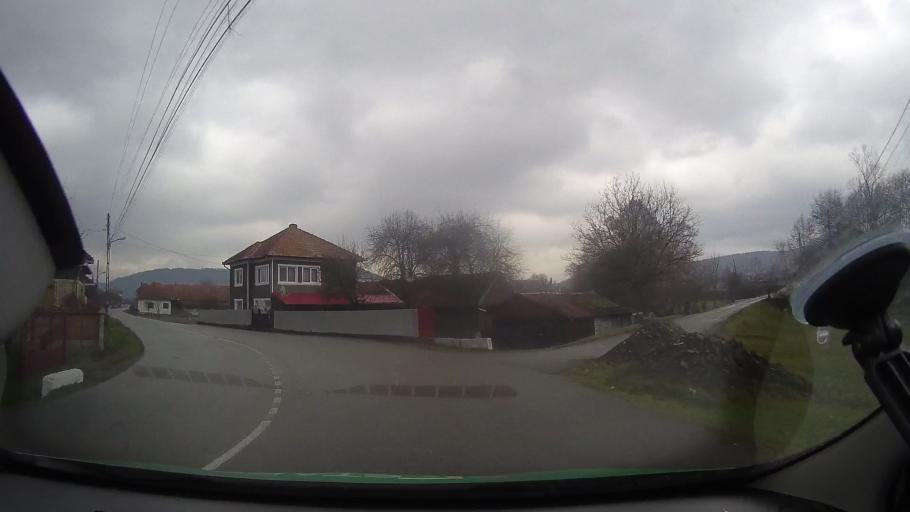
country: RO
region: Hunedoara
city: Vata de Jos
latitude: 46.1897
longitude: 22.6207
